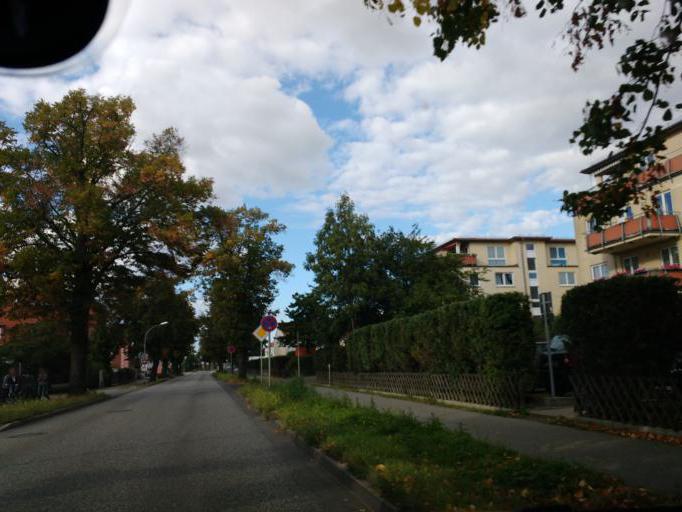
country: DE
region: Berlin
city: Lichtenrade
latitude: 52.3998
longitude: 13.4417
